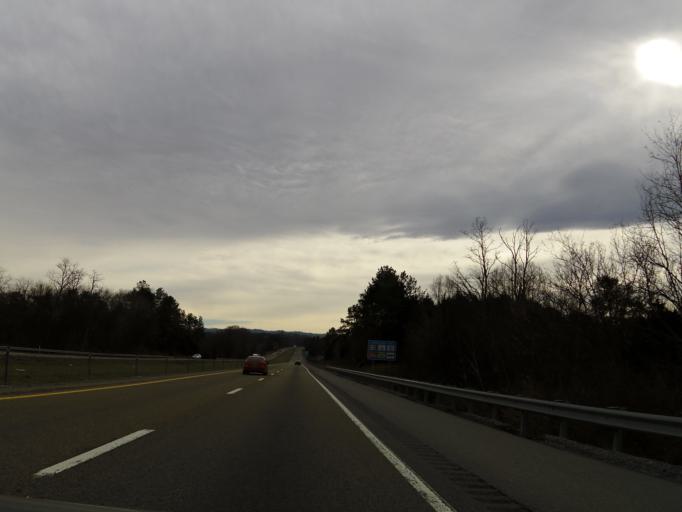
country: US
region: Tennessee
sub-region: Cocke County
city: Newport
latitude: 35.9648
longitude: -83.2201
